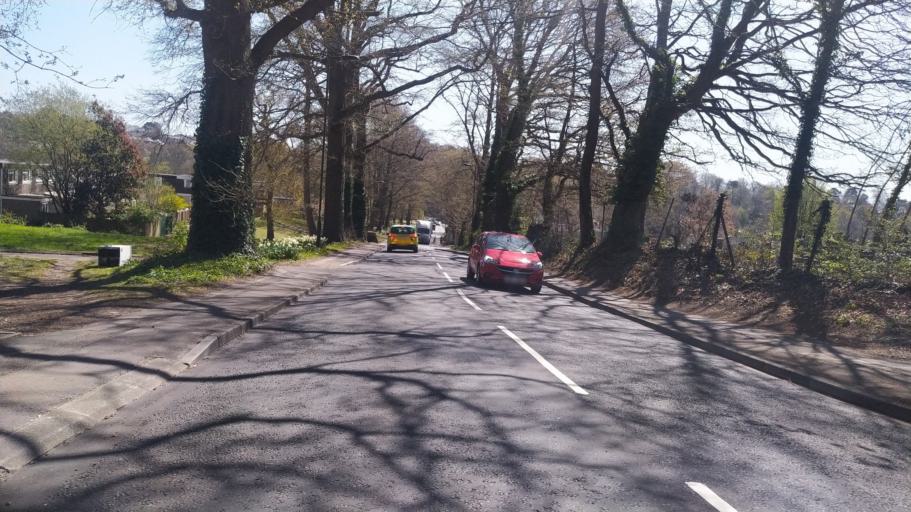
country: GB
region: England
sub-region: Southampton
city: Southampton
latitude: 50.9392
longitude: -1.4270
